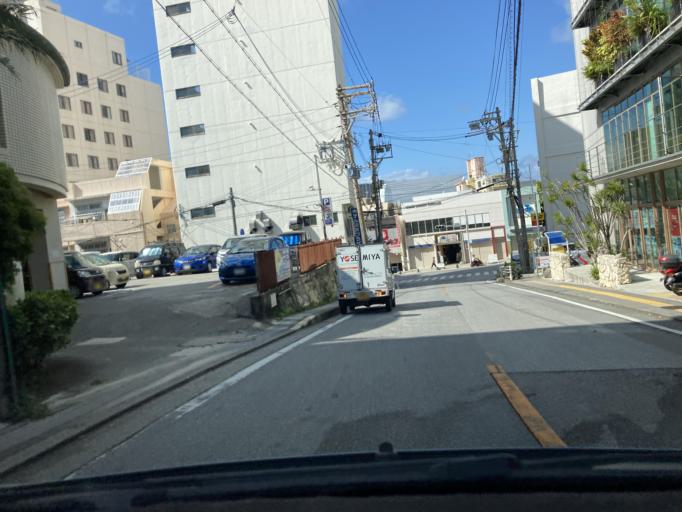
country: JP
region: Okinawa
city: Naha-shi
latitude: 26.2143
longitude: 127.6841
